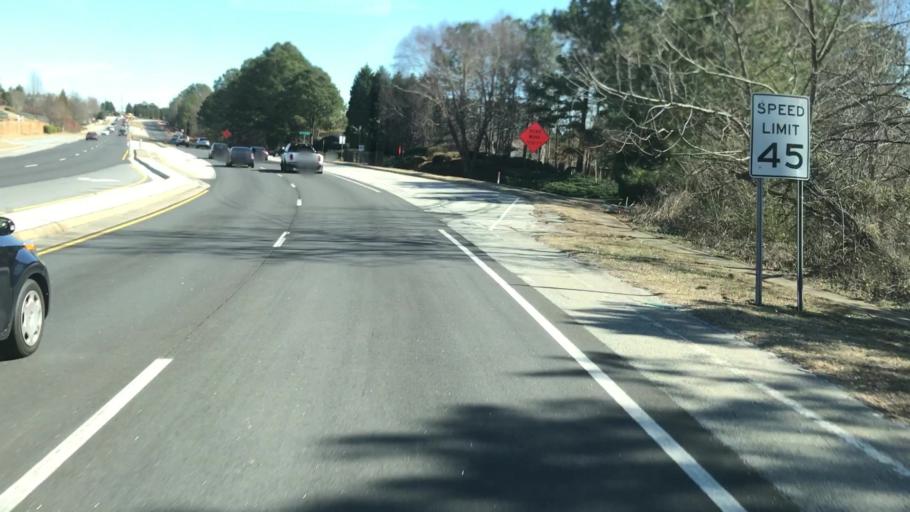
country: US
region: Georgia
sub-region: Gwinnett County
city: Lawrenceville
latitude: 33.9201
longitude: -84.0142
